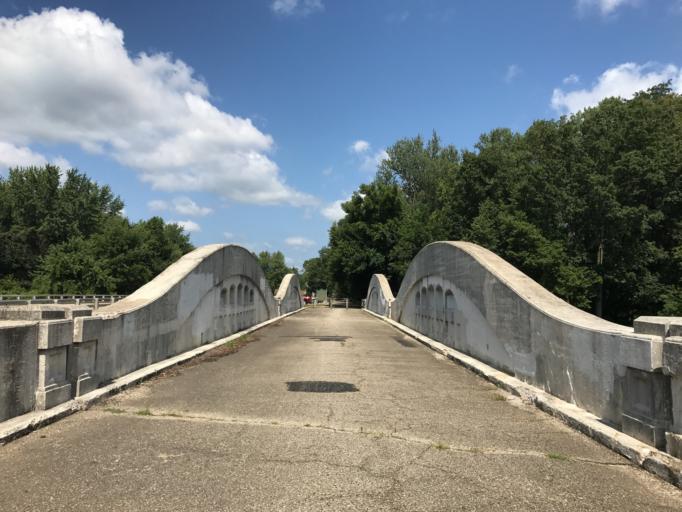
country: US
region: Michigan
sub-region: Saint Joseph County
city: Constantine
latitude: 41.7999
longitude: -85.7568
